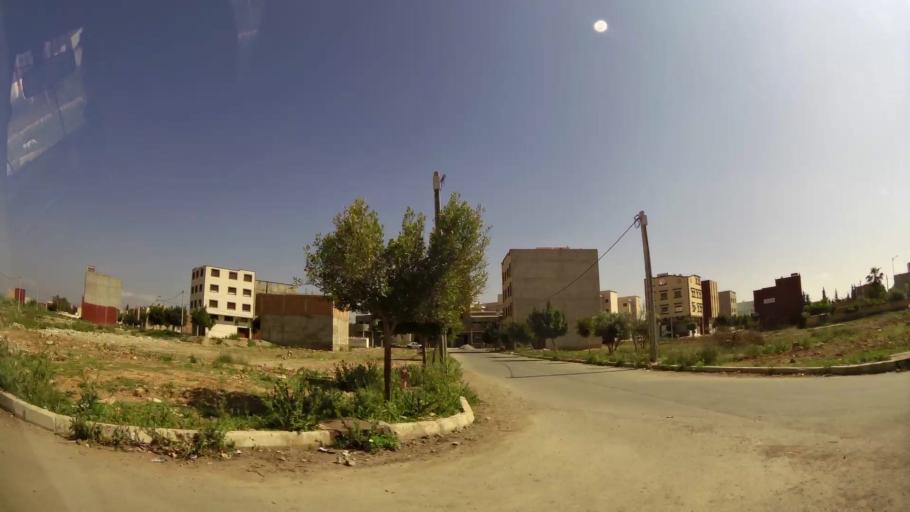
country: MA
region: Oriental
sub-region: Oujda-Angad
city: Oujda
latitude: 34.6983
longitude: -1.8773
